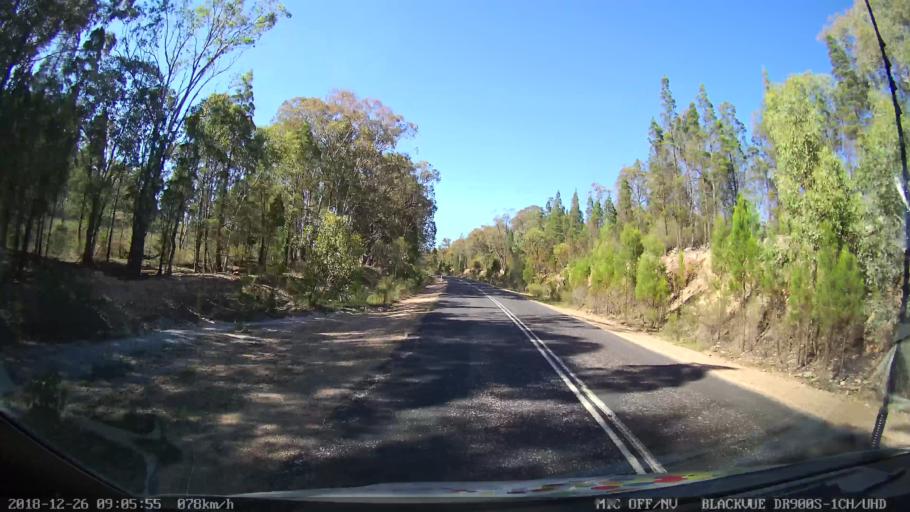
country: AU
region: New South Wales
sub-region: Mid-Western Regional
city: Kandos
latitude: -32.6880
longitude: 150.0049
